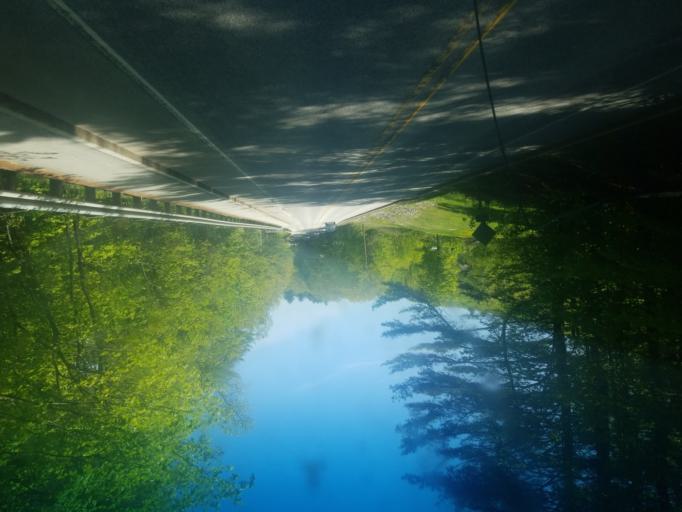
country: US
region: New Hampshire
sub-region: Grafton County
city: Plymouth
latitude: 43.7643
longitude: -71.7118
